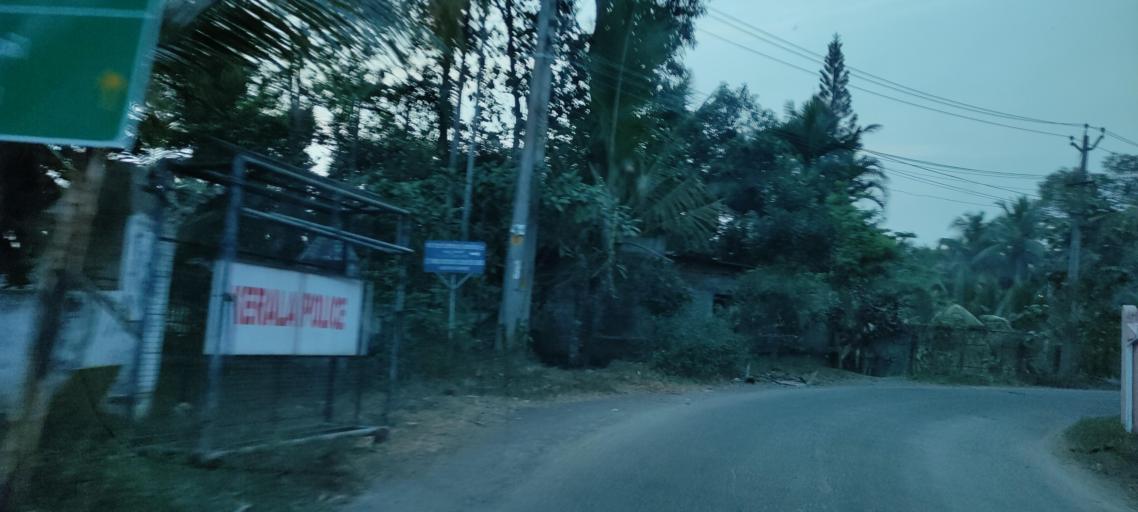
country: IN
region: Kerala
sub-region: Pattanamtitta
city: Tiruvalla
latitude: 9.3312
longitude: 76.5155
